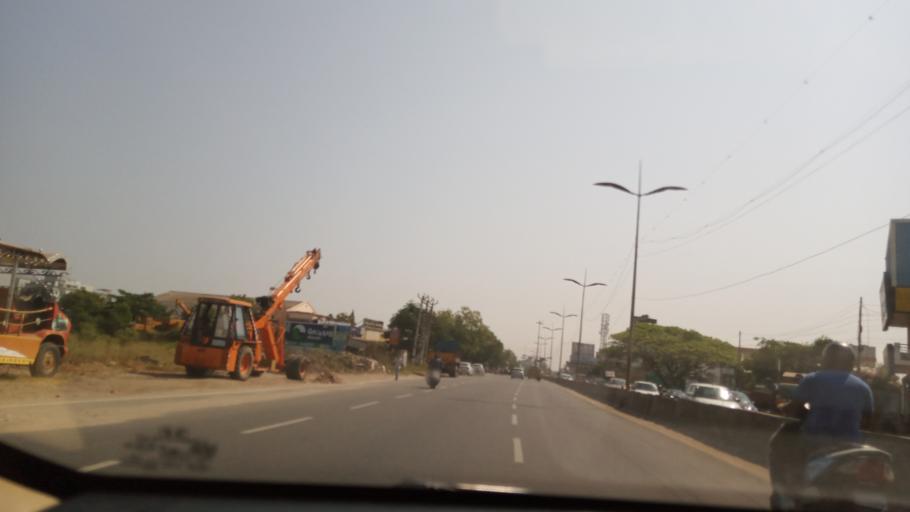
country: IN
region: Tamil Nadu
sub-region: Coimbatore
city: Irugur
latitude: 11.0430
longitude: 77.0447
